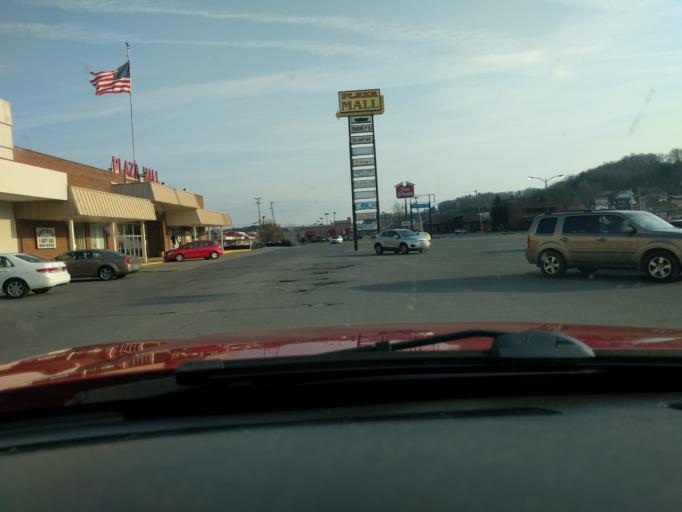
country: US
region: West Virginia
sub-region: Raleigh County
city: Prosperity
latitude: 37.8118
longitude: -81.1846
